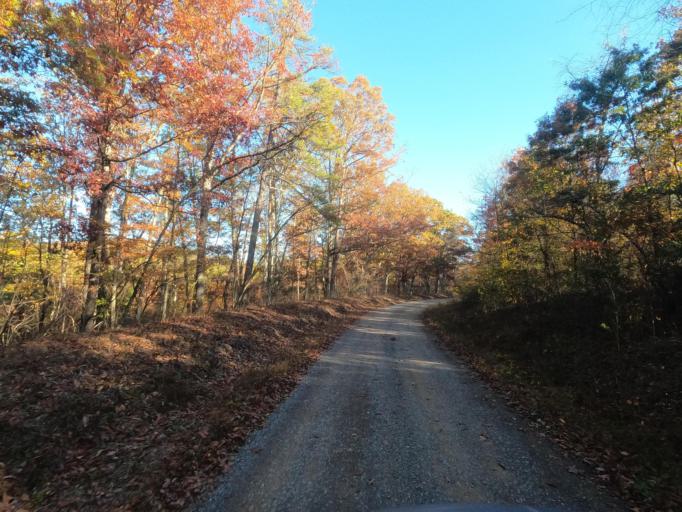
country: US
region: West Virginia
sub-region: Mineral County
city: Fort Ashby
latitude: 39.5462
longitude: -78.5294
